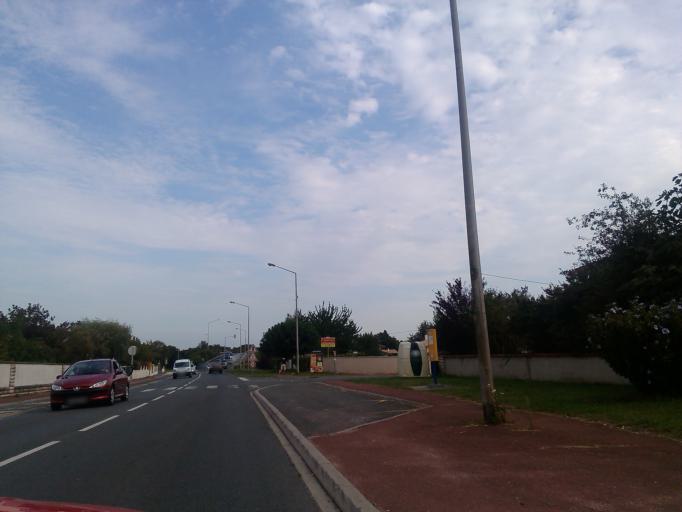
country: FR
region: Poitou-Charentes
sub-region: Departement de la Charente-Maritime
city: Saujon
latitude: 45.6744
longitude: -0.9438
